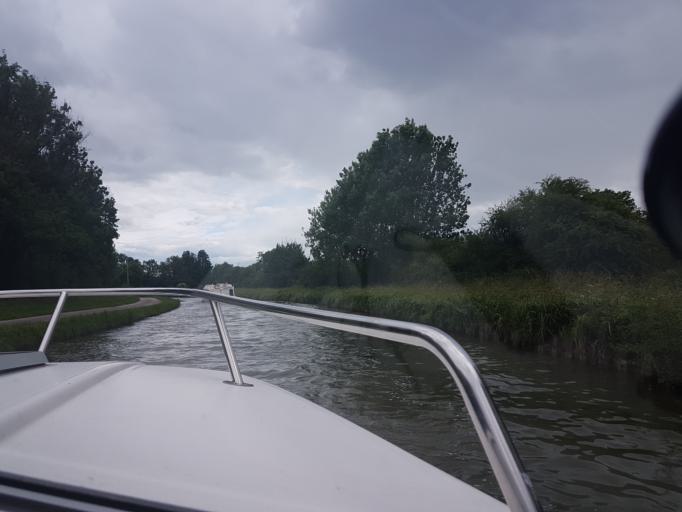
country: FR
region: Bourgogne
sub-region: Departement de l'Yonne
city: Vermenton
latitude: 47.5524
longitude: 3.6314
